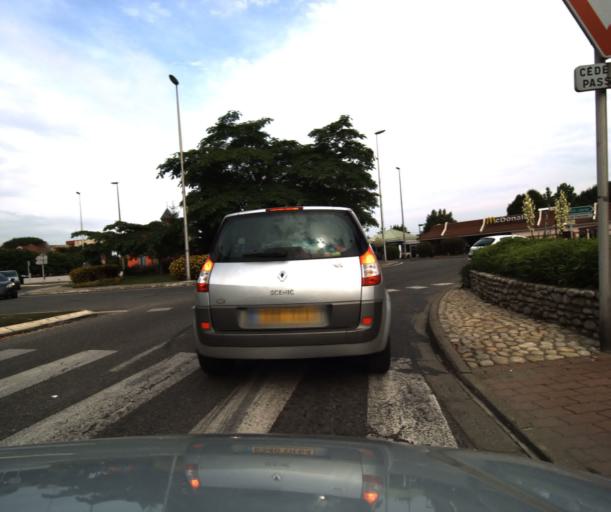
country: FR
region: Midi-Pyrenees
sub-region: Departement des Hautes-Pyrenees
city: Laloubere
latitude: 43.2211
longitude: 0.0614
